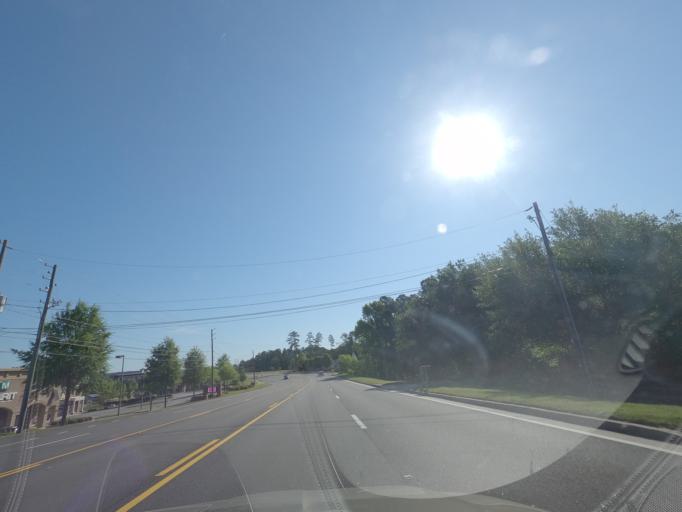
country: US
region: Georgia
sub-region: Columbia County
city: Evans
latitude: 33.5278
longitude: -82.1336
